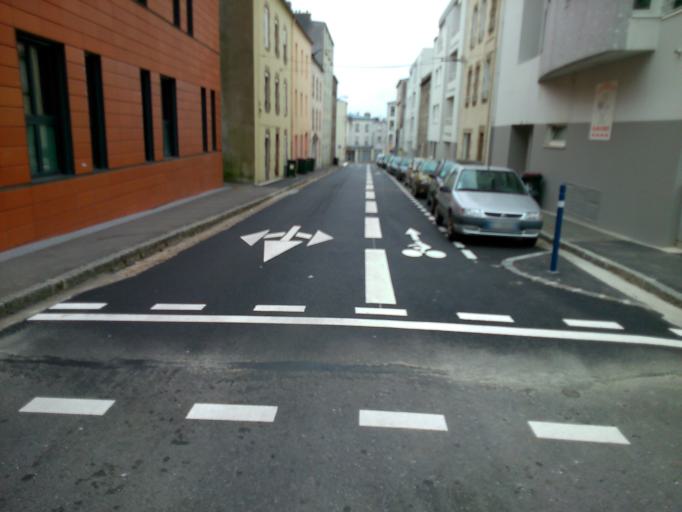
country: FR
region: Brittany
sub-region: Departement du Finistere
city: Brest
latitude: 48.3977
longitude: -4.4727
